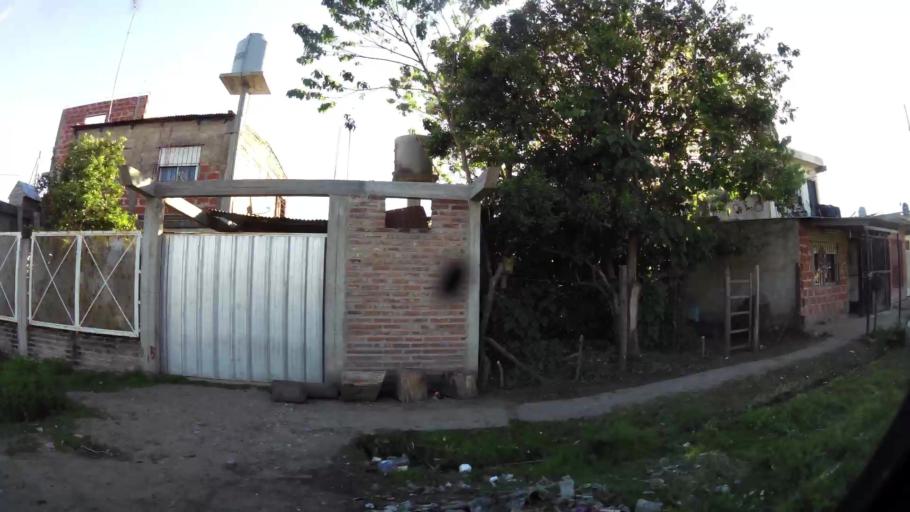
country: AR
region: Buenos Aires
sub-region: Partido de Almirante Brown
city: Adrogue
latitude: -34.7670
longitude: -58.3309
